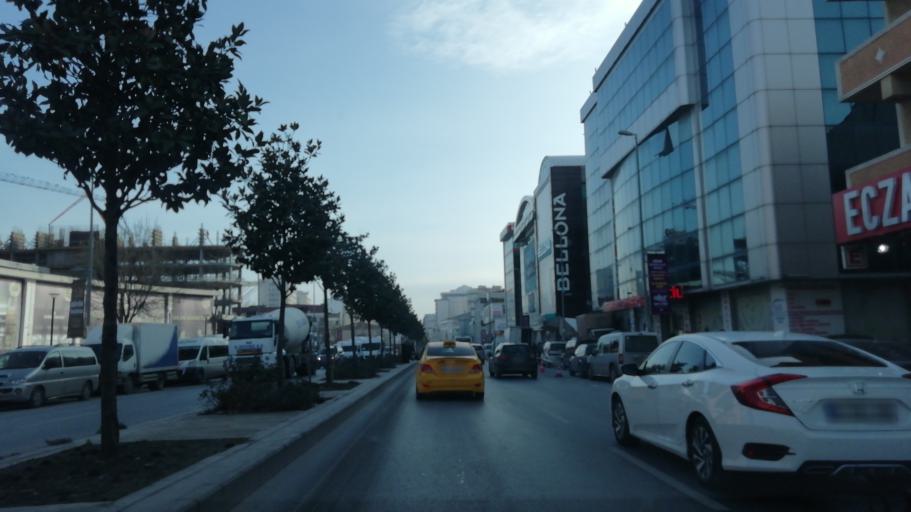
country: TR
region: Istanbul
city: Esenyurt
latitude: 41.0452
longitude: 28.6749
